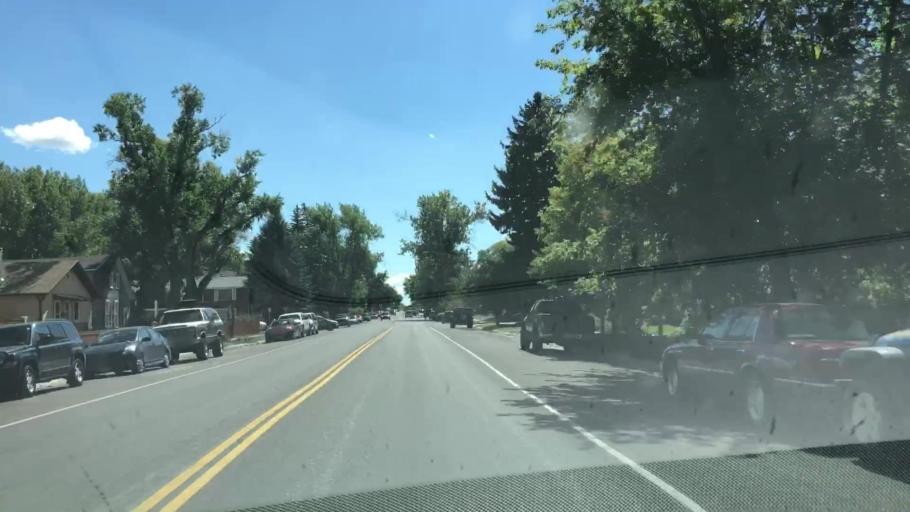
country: US
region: Wyoming
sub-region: Albany County
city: Laramie
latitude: 41.3179
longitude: -105.5850
